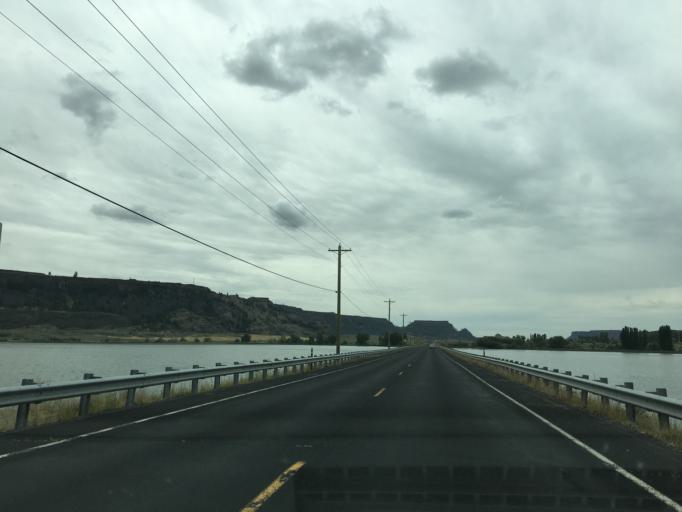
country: US
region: Washington
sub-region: Okanogan County
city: Coulee Dam
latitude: 47.9253
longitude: -119.0483
